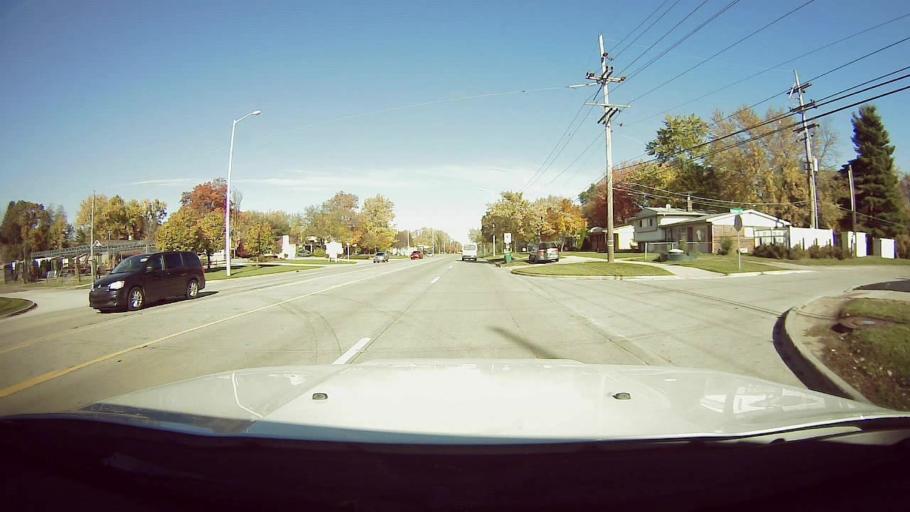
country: US
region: Michigan
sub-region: Oakland County
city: Farmington
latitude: 42.4421
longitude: -83.3753
